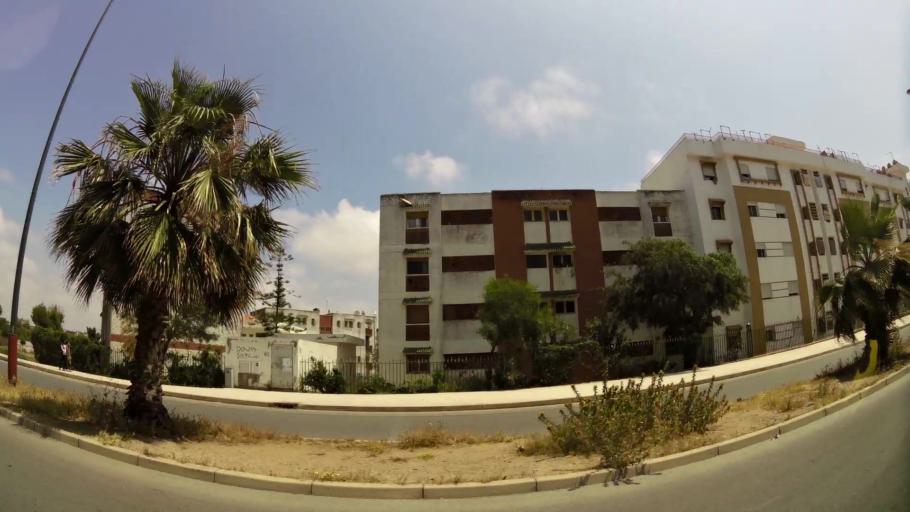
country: MA
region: Rabat-Sale-Zemmour-Zaer
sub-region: Skhirate-Temara
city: Temara
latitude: 33.9716
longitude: -6.8968
